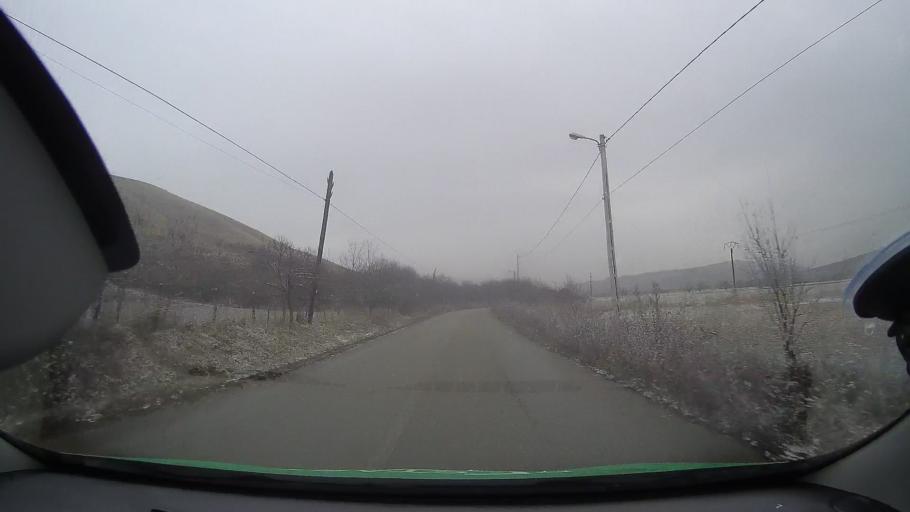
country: RO
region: Alba
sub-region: Comuna Noslac
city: Noslac
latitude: 46.3390
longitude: 23.9517
